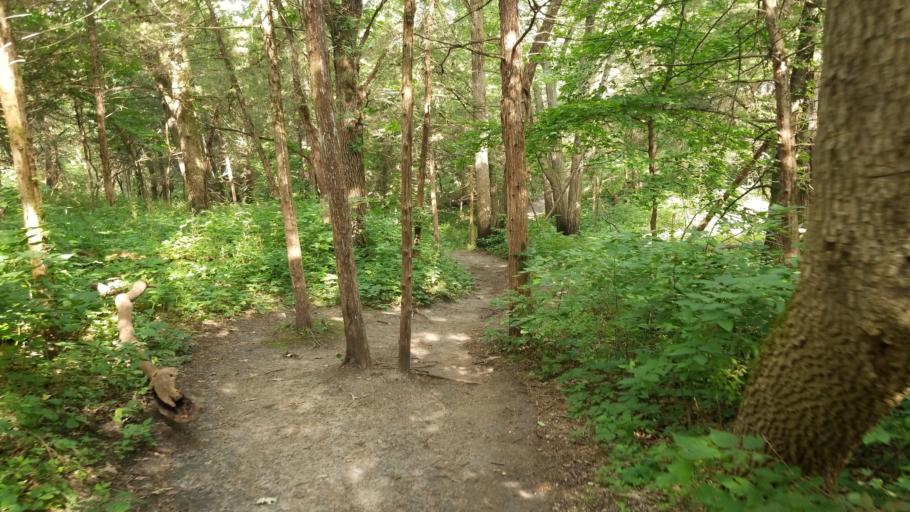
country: US
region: Nebraska
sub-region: Cass County
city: Louisville
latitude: 41.0248
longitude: -96.2502
